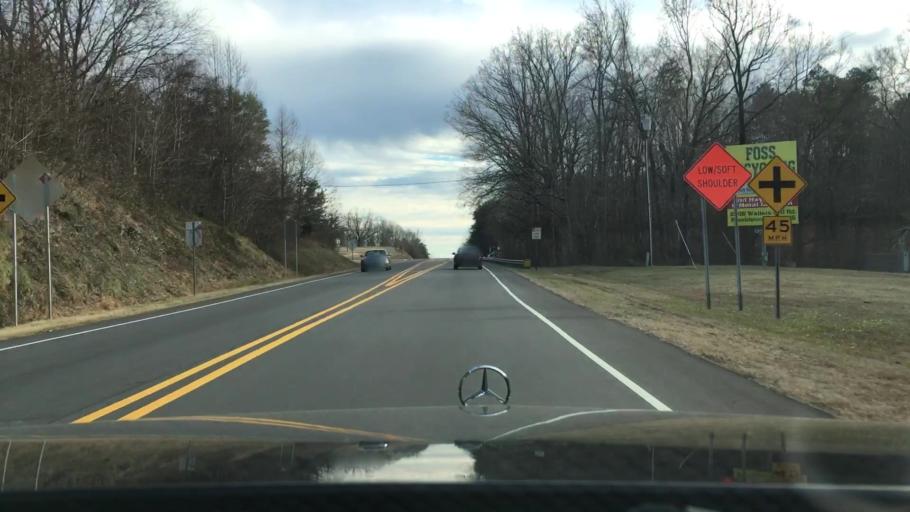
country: US
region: Virginia
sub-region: City of Danville
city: Danville
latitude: 36.4906
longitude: -79.3838
